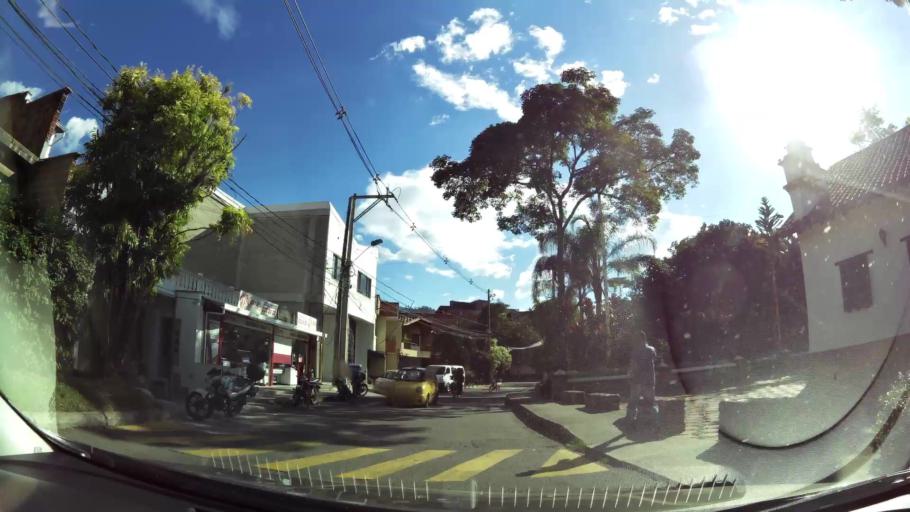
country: CO
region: Antioquia
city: Envigado
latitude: 6.1726
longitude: -75.5790
